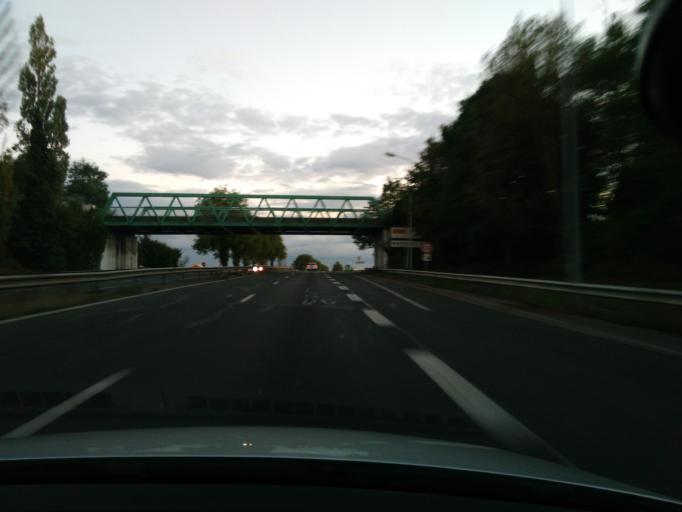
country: FR
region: Ile-de-France
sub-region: Departement de Seine-et-Marne
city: Nanteuil-les-Meaux
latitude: 48.9286
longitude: 2.8803
